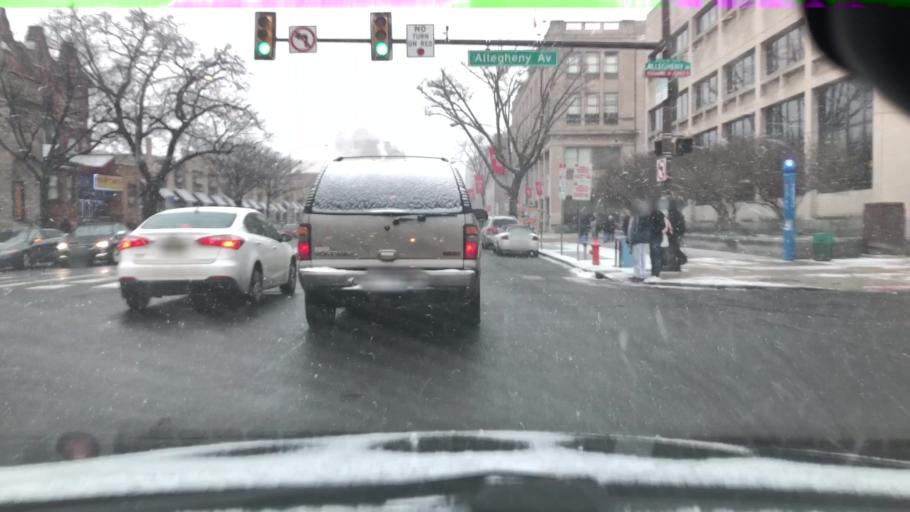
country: US
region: Pennsylvania
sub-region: Philadelphia County
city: Philadelphia
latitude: 40.0014
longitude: -75.1529
